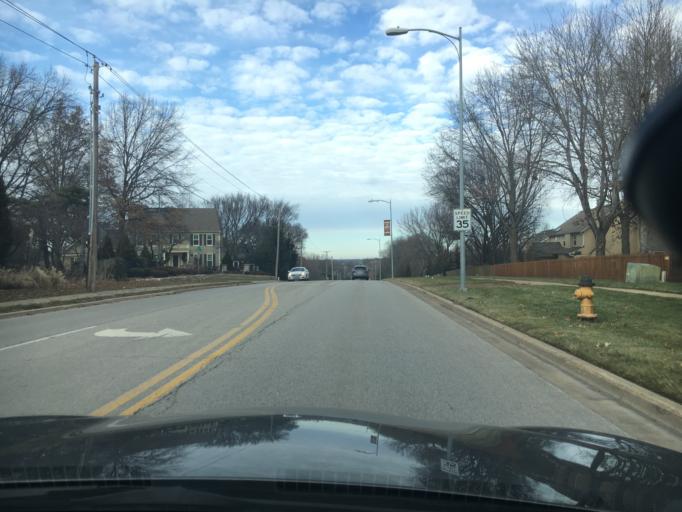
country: US
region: Kansas
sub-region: Johnson County
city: Leawood
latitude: 38.8989
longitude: -94.6305
